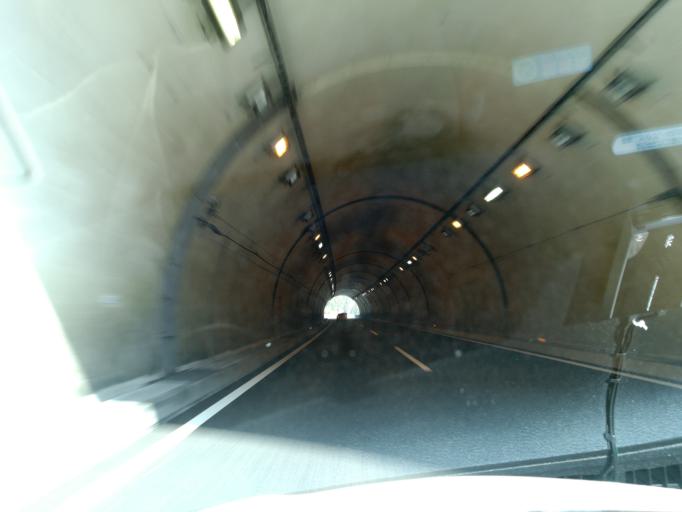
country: JP
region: Ehime
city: Kawanoecho
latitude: 33.8274
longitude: 133.6604
